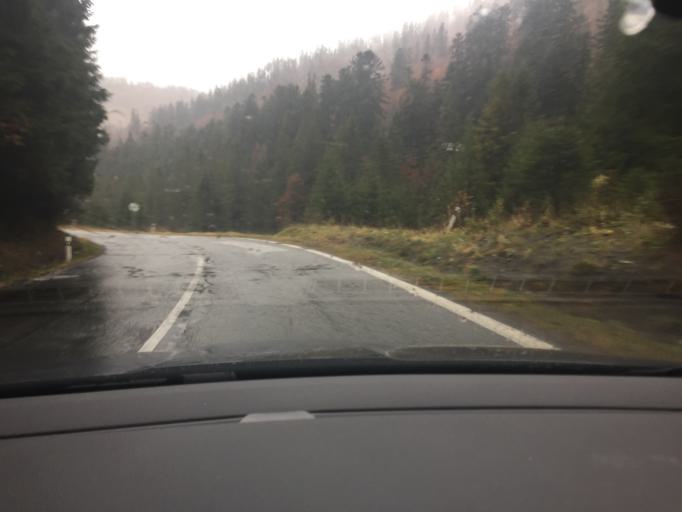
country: SK
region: Presovsky
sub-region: Okres Poprad
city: Zdiar
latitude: 49.2578
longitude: 20.3022
